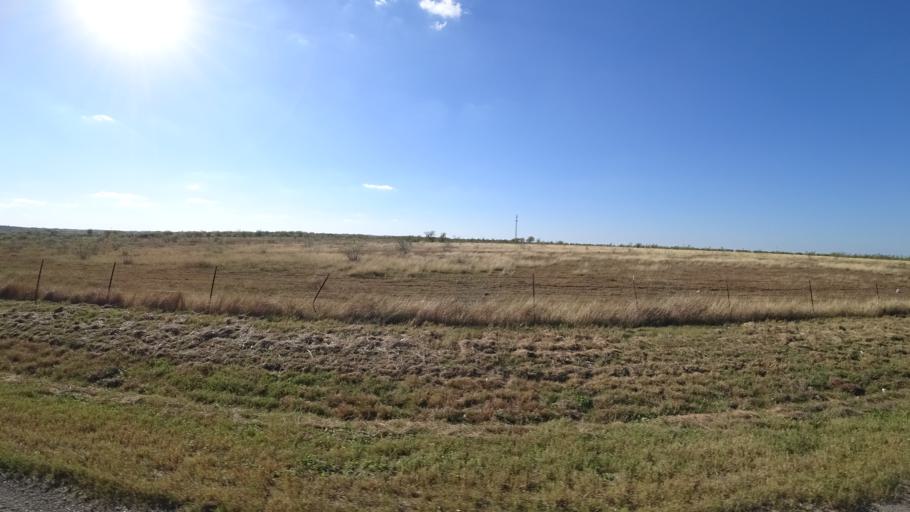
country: US
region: Texas
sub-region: Travis County
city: Onion Creek
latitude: 30.1361
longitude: -97.6963
